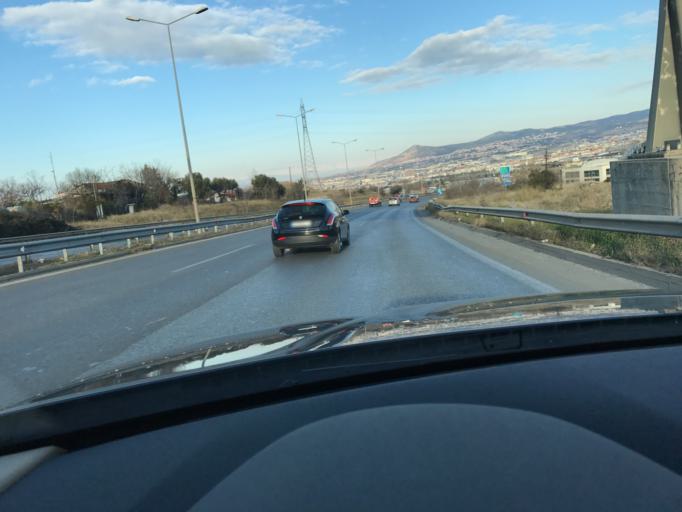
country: GR
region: Central Macedonia
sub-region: Nomos Thessalonikis
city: Polichni
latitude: 40.6653
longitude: 22.9645
